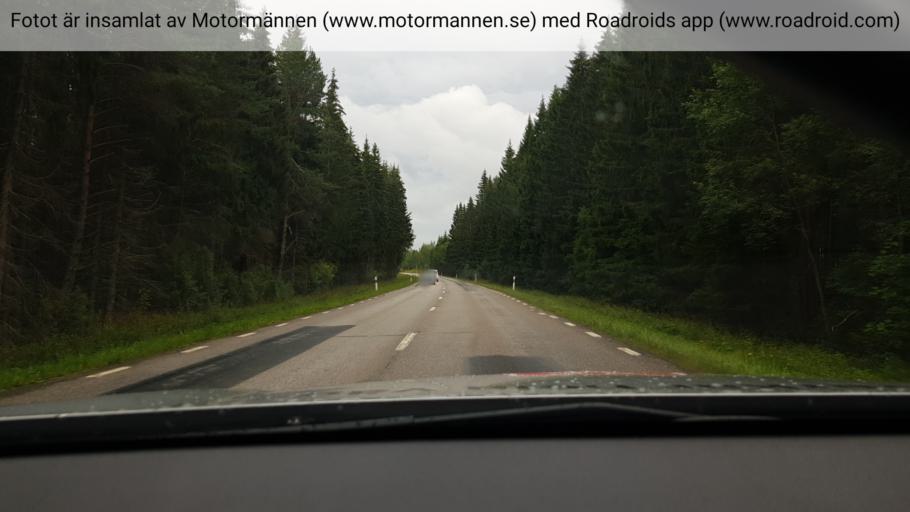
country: SE
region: Uppsala
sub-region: Alvkarleby Kommun
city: AElvkarleby
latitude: 60.5591
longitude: 17.4669
